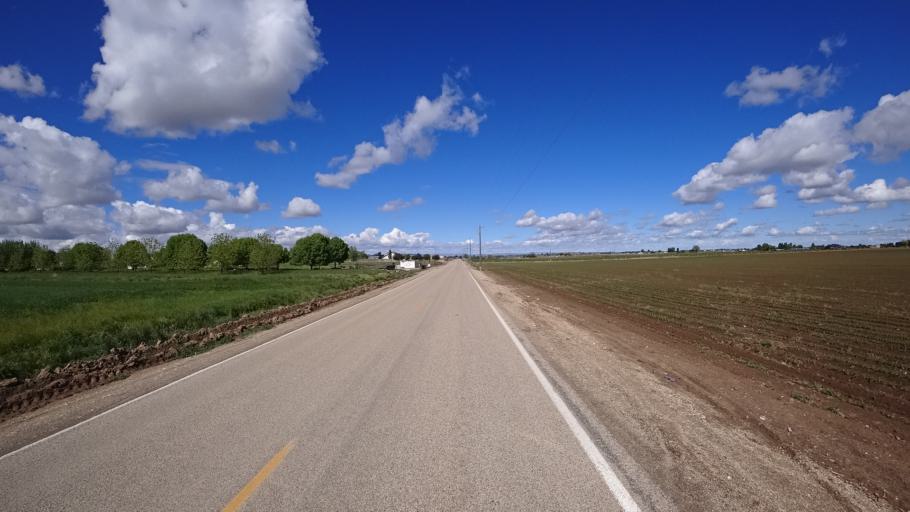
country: US
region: Idaho
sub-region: Ada County
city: Kuna
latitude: 43.4664
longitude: -116.4558
